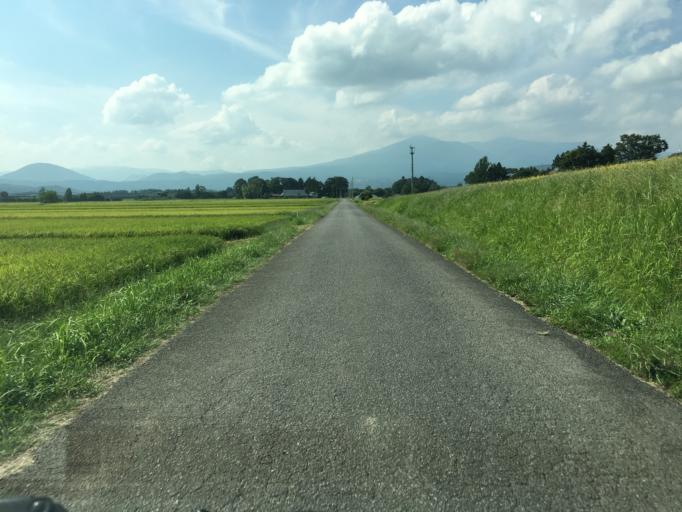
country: JP
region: Fukushima
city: Motomiya
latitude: 37.5316
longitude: 140.3903
